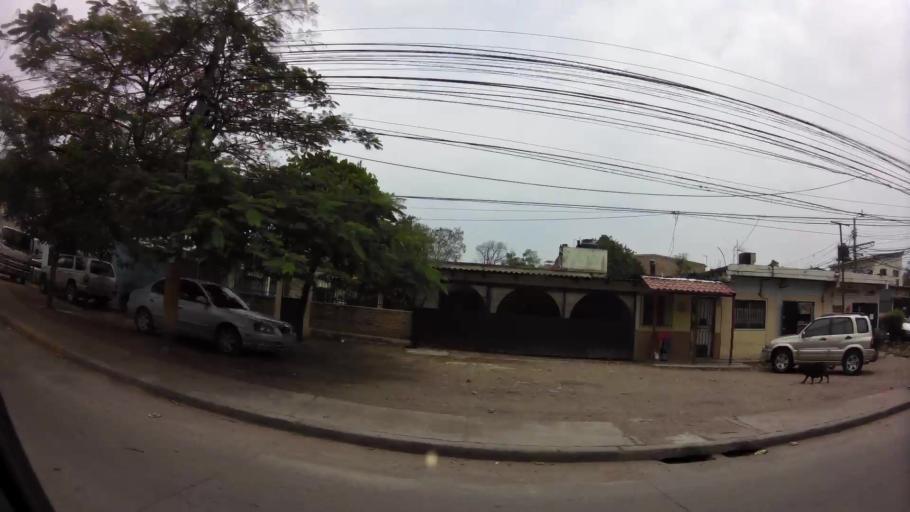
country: HN
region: Francisco Morazan
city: Tegucigalpa
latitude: 14.0632
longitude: -87.1987
